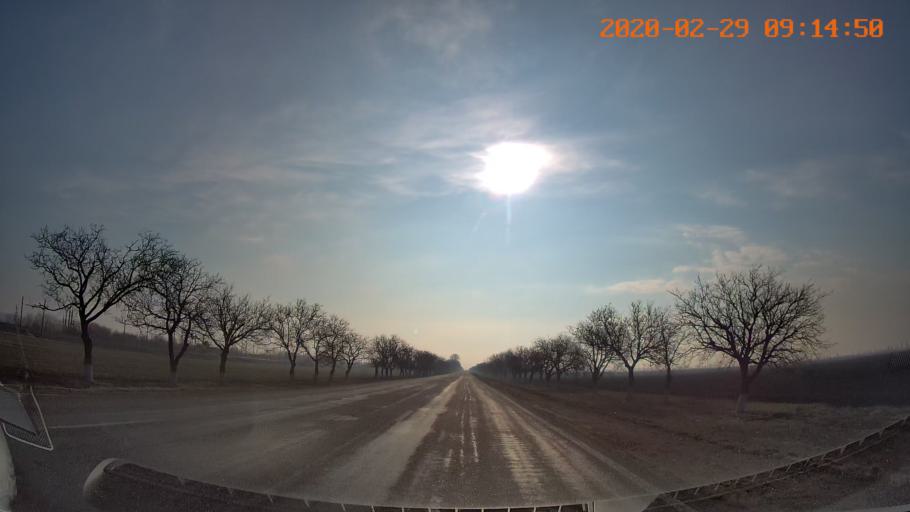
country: MD
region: Telenesti
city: Pervomaisc
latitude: 46.8053
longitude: 29.8595
